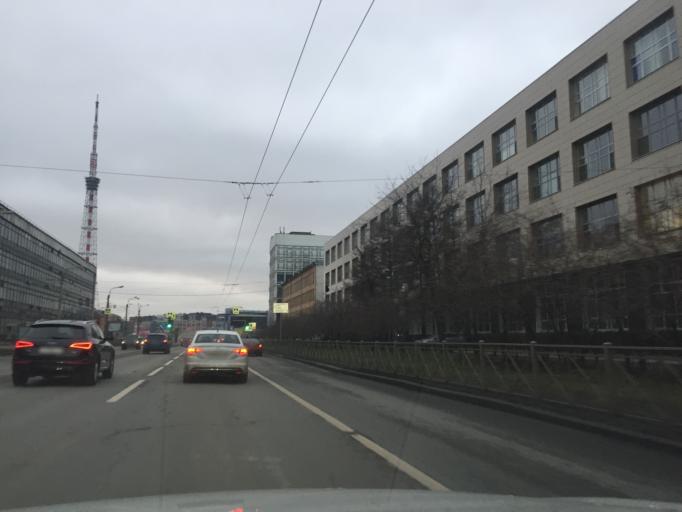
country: RU
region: Leningrad
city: Sampsonievskiy
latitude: 59.9822
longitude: 30.3296
